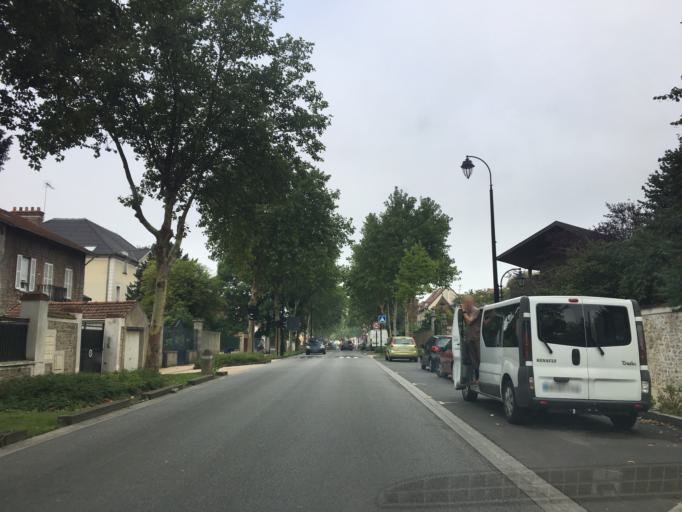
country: FR
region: Ile-de-France
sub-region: Departement de Seine-et-Marne
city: Brie-Comte-Robert
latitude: 48.6949
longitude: 2.6097
